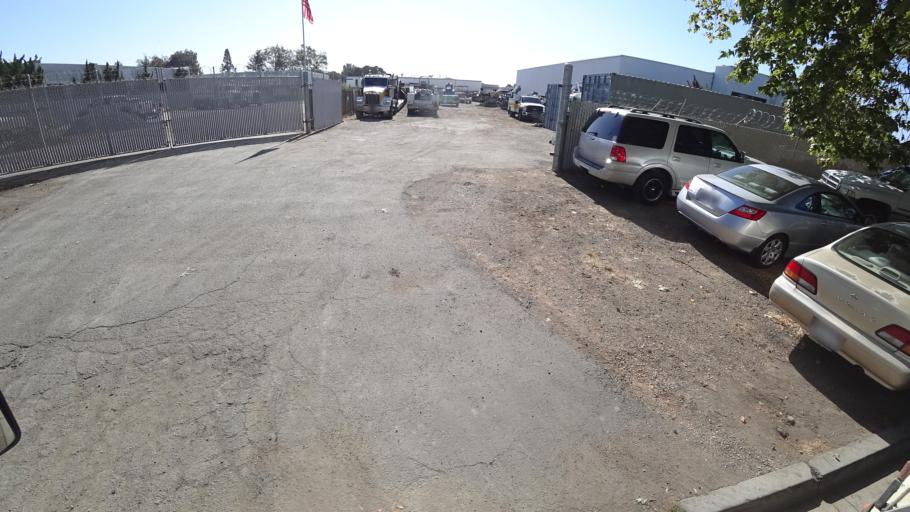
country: US
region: California
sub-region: Alameda County
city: San Lorenzo
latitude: 37.6408
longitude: -122.1313
